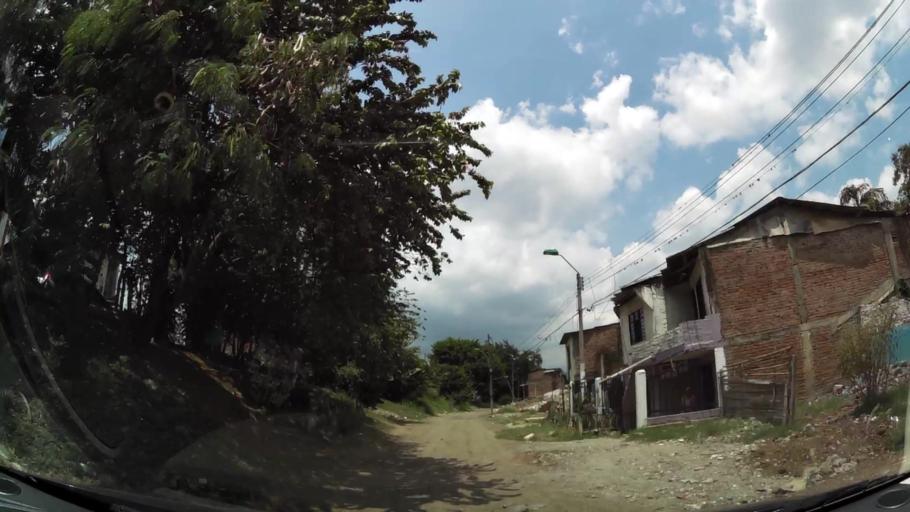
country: CO
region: Valle del Cauca
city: Cali
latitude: 3.4510
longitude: -76.4773
